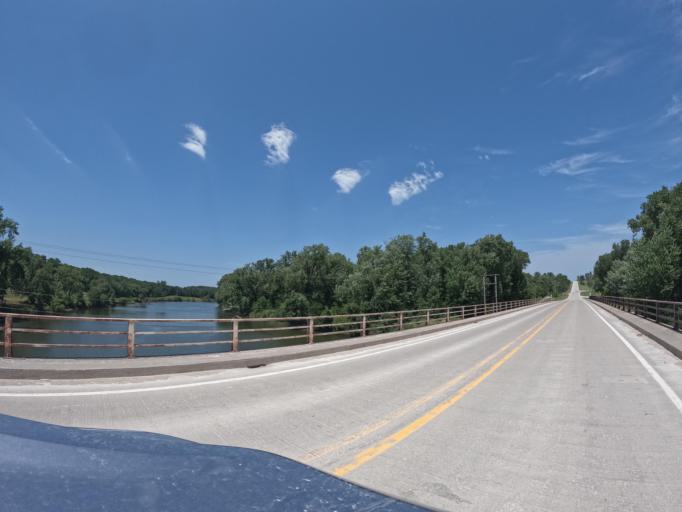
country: US
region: Iowa
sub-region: Henry County
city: Mount Pleasant
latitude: 40.9360
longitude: -91.6190
